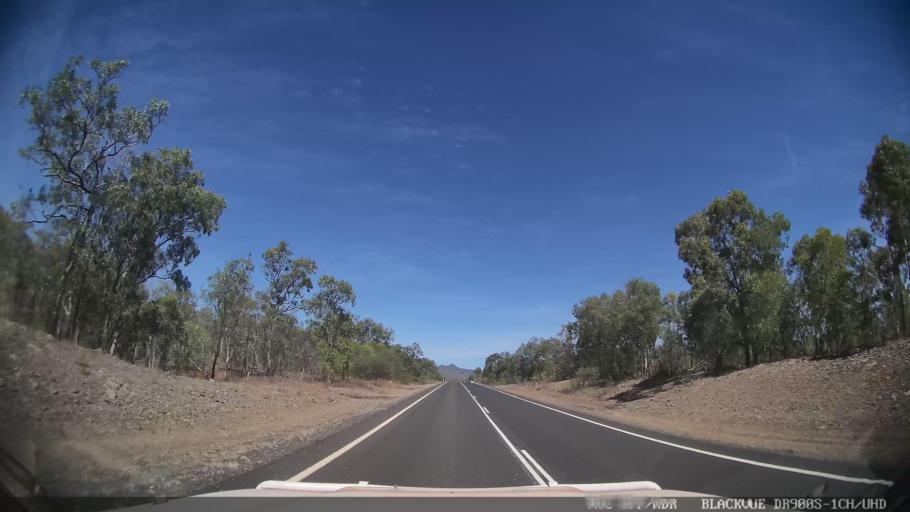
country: AU
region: Queensland
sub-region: Cook
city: Cooktown
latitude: -15.7033
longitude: 144.6079
